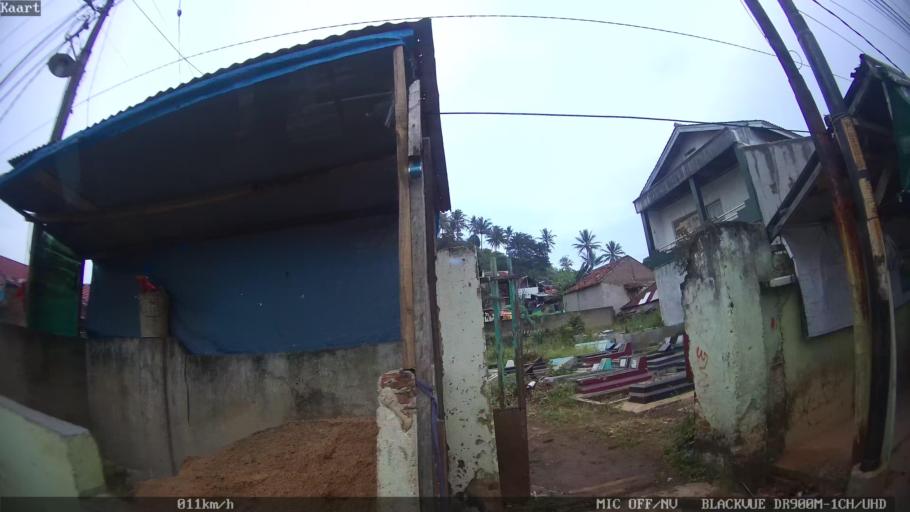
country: ID
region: Lampung
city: Bandarlampung
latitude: -5.4135
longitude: 105.2509
